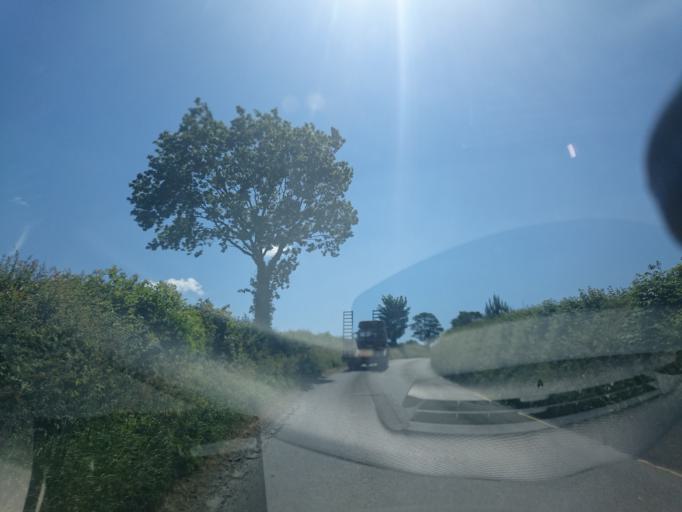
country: IE
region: Leinster
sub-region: Kilkenny
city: Graiguenamanagh
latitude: 52.6085
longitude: -6.9929
